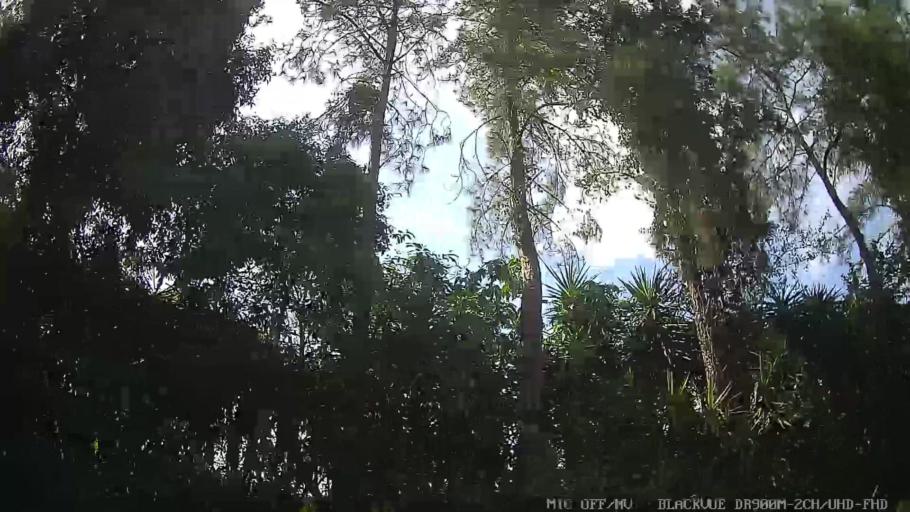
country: BR
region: Sao Paulo
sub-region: Cosmopolis
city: Cosmopolis
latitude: -22.6403
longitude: -47.0892
